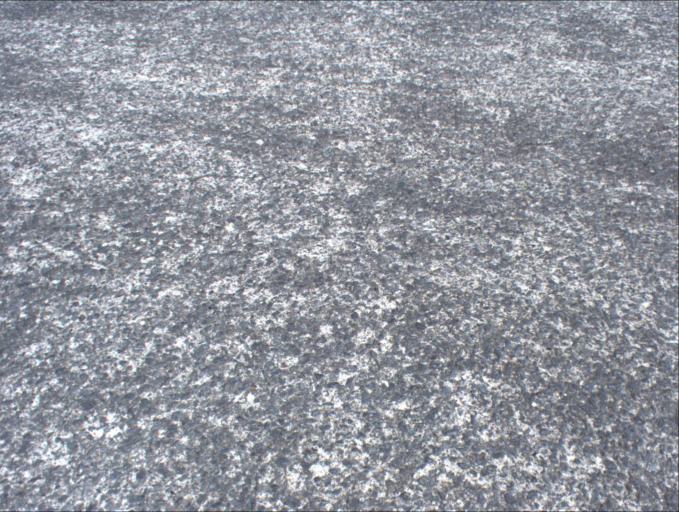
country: AU
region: Queensland
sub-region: Logan
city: Windaroo
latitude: -27.7269
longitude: 153.2065
